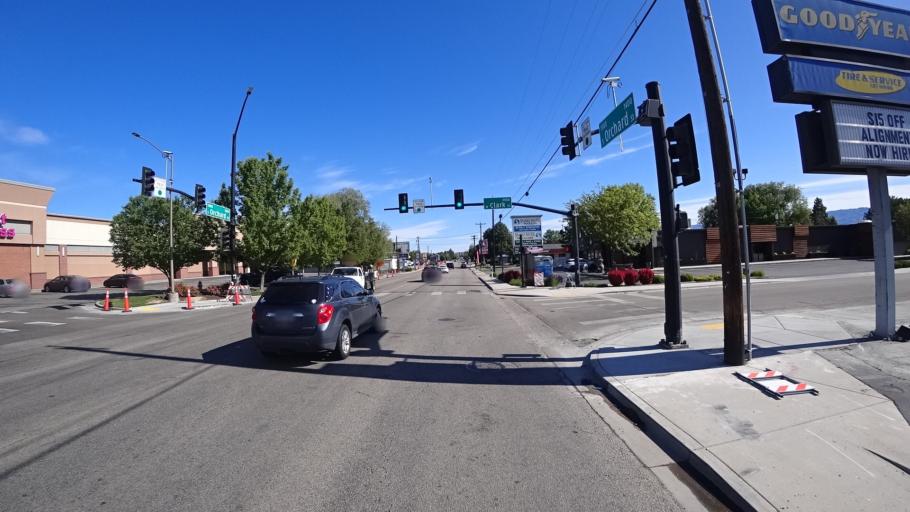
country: US
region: Idaho
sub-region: Ada County
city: Garden City
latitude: 43.5914
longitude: -116.2436
